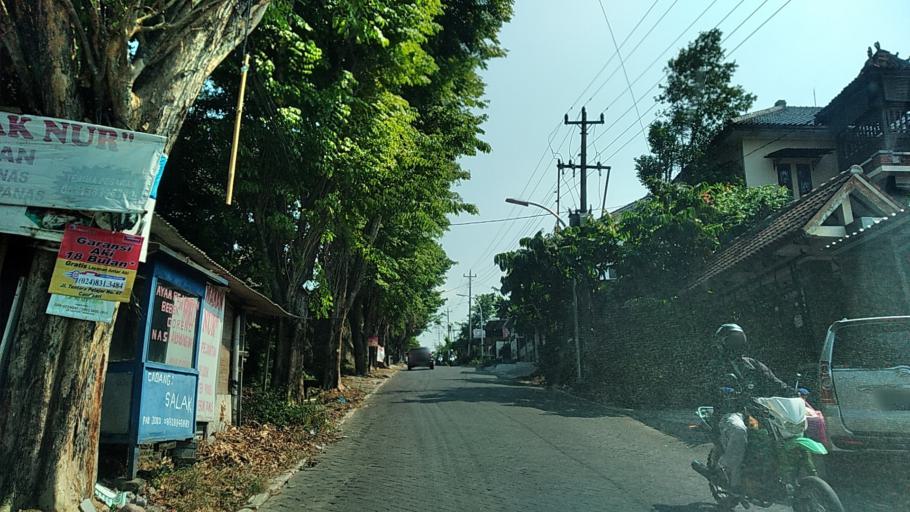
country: ID
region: Central Java
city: Mranggen
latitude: -7.0410
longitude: 110.4758
